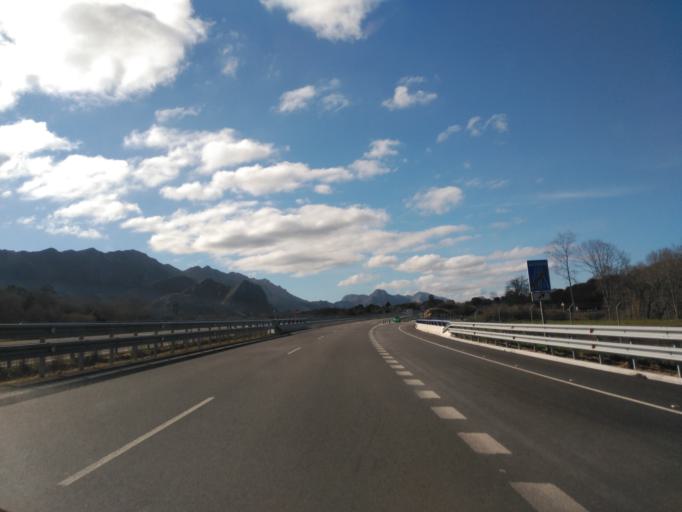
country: ES
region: Asturias
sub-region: Province of Asturias
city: Llanes
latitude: 43.3986
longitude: -4.7122
